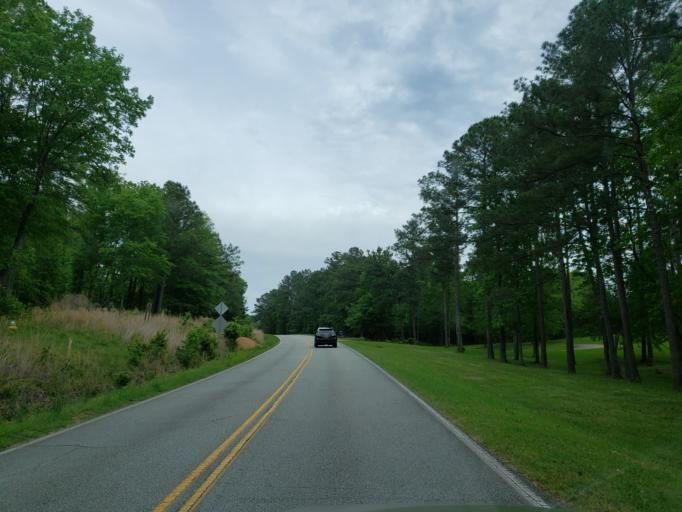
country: US
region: Georgia
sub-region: Bibb County
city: West Point
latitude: 32.8163
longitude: -83.8564
